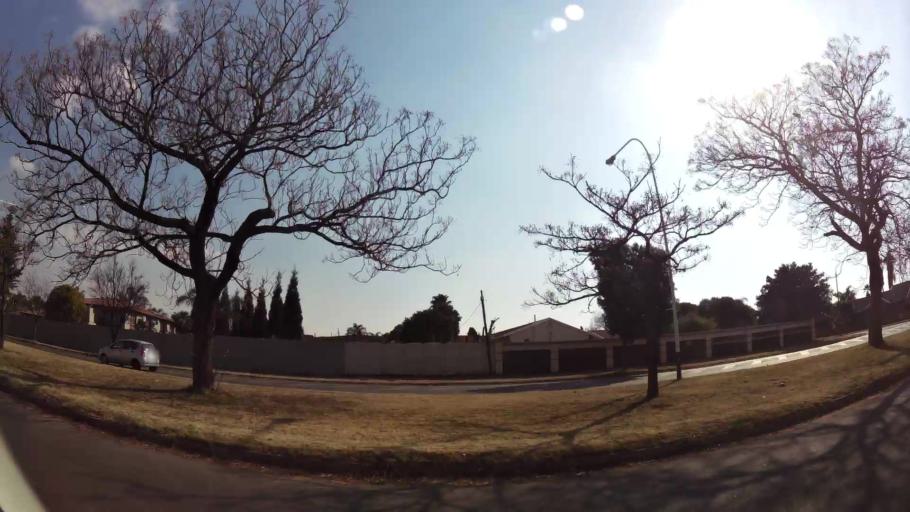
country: ZA
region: Gauteng
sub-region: Ekurhuleni Metropolitan Municipality
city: Boksburg
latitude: -26.1836
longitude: 28.2660
